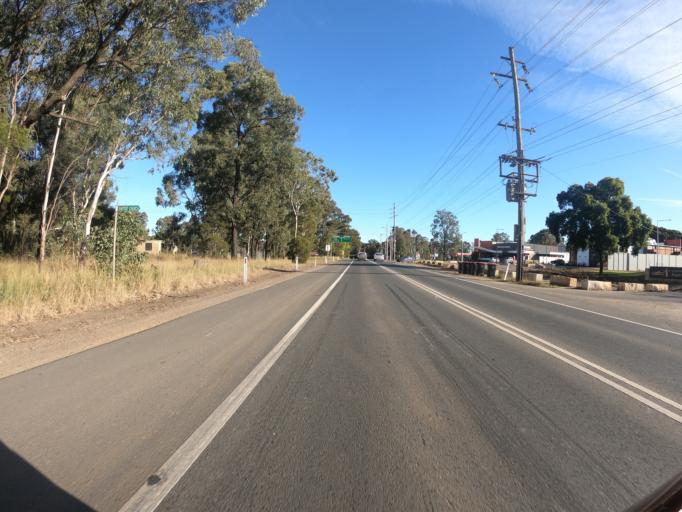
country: AU
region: New South Wales
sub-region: Hawkesbury
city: South Windsor
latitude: -33.6379
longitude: 150.7859
